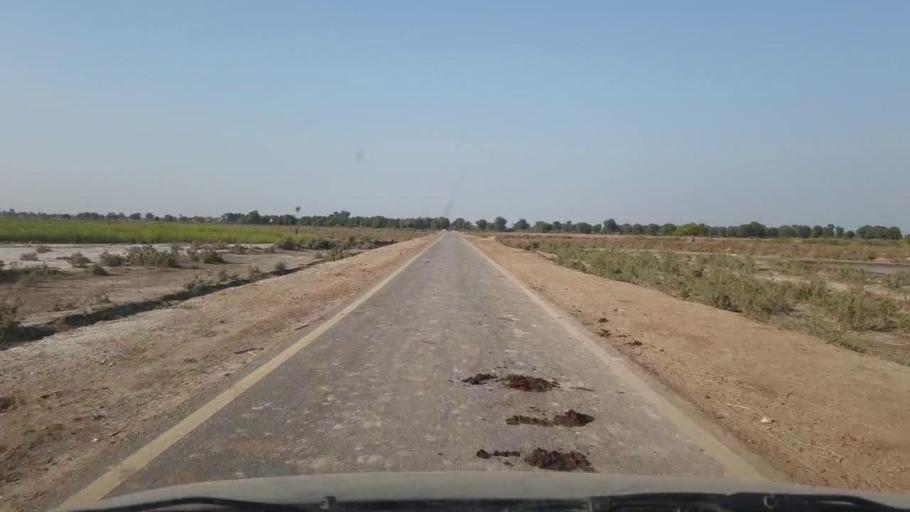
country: PK
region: Sindh
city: Samaro
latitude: 25.2938
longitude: 69.3491
